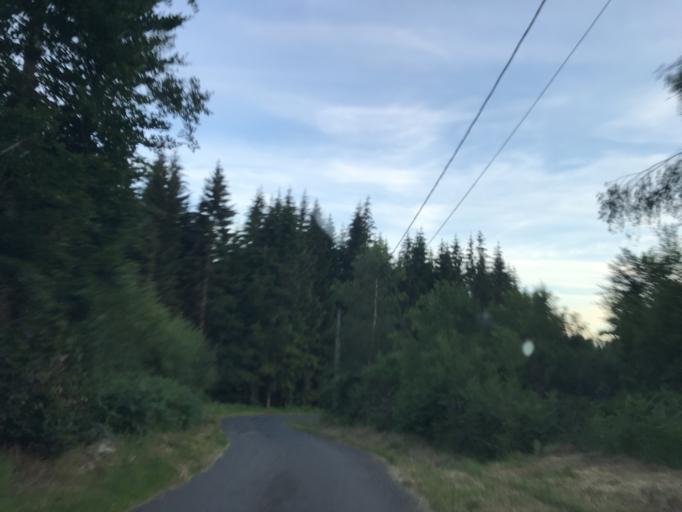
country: FR
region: Rhone-Alpes
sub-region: Departement de la Loire
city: Noiretable
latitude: 45.7993
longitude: 3.7030
